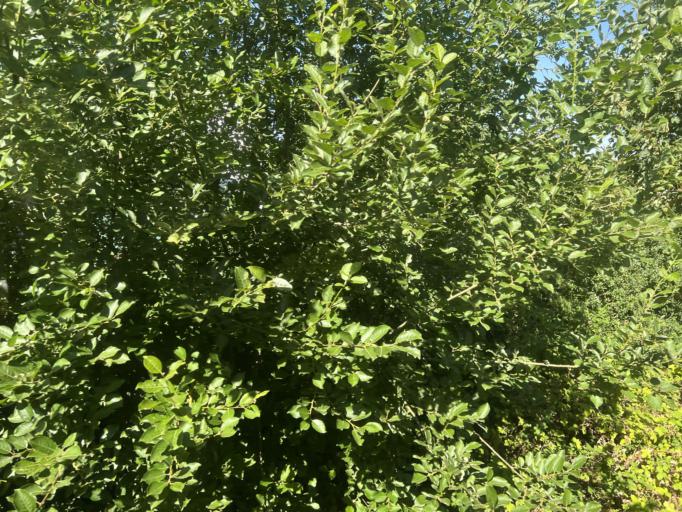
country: GB
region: England
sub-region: Lincolnshire
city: Boston
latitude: 52.9802
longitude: -0.0306
